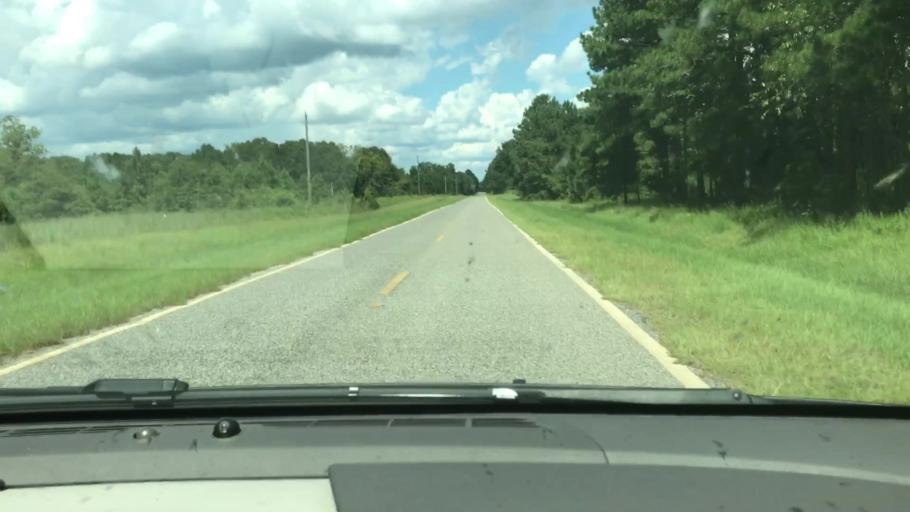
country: US
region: Georgia
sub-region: Clay County
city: Fort Gaines
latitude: 31.7397
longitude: -85.0870
